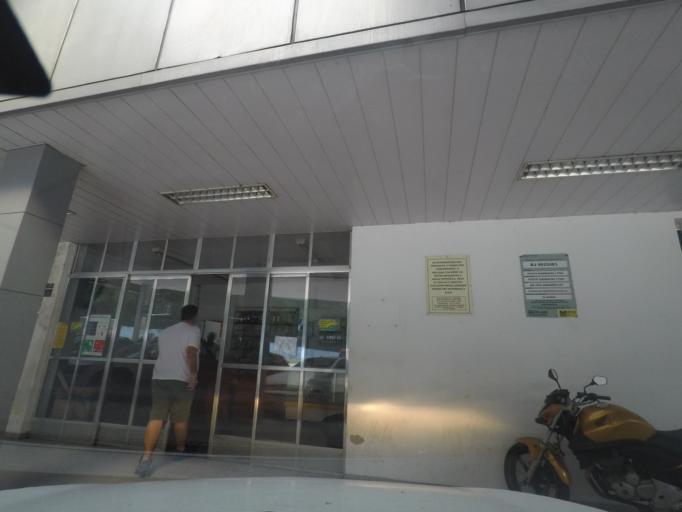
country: BR
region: Rio de Janeiro
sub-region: Guapimirim
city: Guapimirim
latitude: -22.4815
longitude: -42.9959
